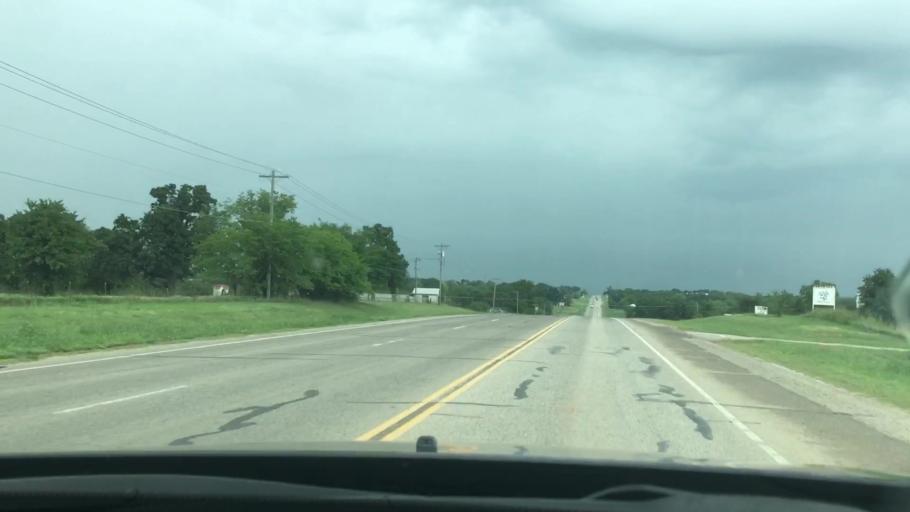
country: US
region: Oklahoma
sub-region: Carter County
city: Healdton
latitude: 34.2021
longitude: -97.4747
